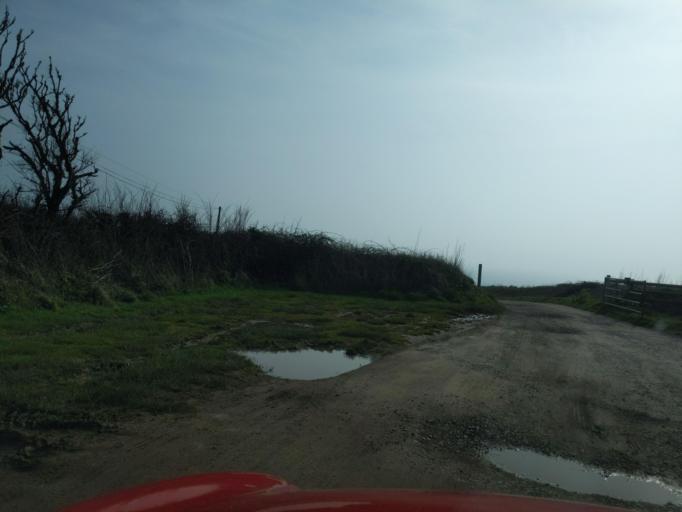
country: GB
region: England
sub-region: Devon
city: Salcombe
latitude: 50.2225
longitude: -3.7510
